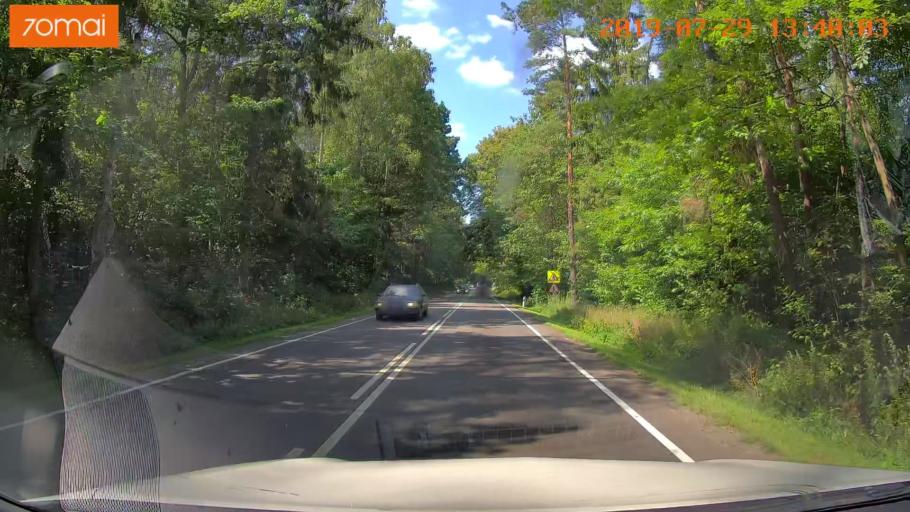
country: RU
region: Kaliningrad
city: Svetlyy
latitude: 54.7260
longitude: 20.1431
